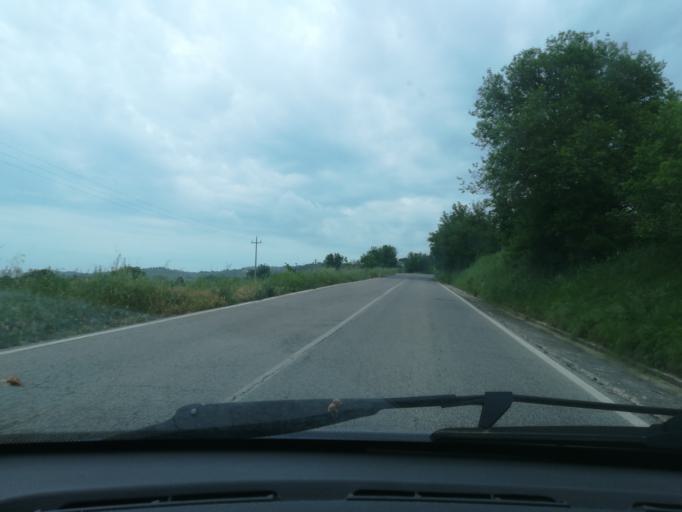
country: IT
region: The Marches
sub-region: Provincia di Macerata
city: Casette Verdini
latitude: 43.2871
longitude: 13.3837
